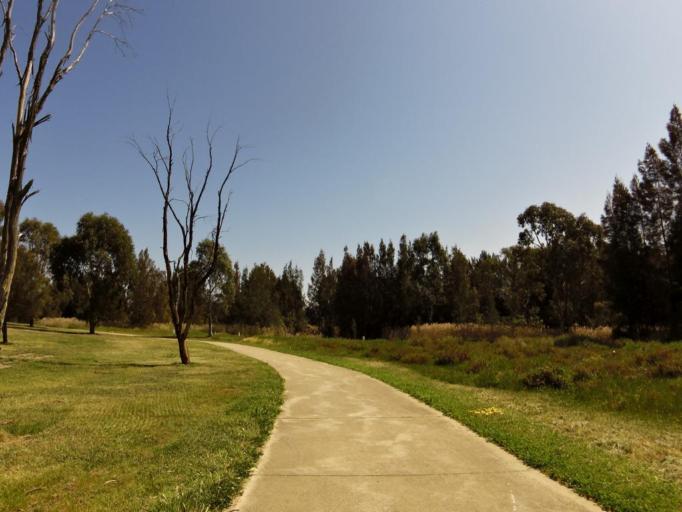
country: AU
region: Victoria
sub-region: Wyndham
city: Williams Landing
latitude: -37.8756
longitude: 144.7400
